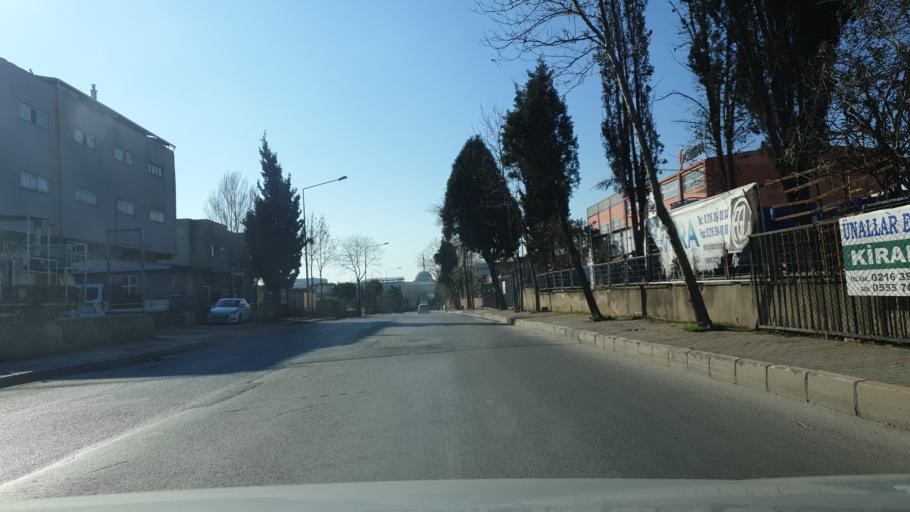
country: TR
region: Istanbul
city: Icmeler
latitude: 40.8782
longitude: 29.3623
